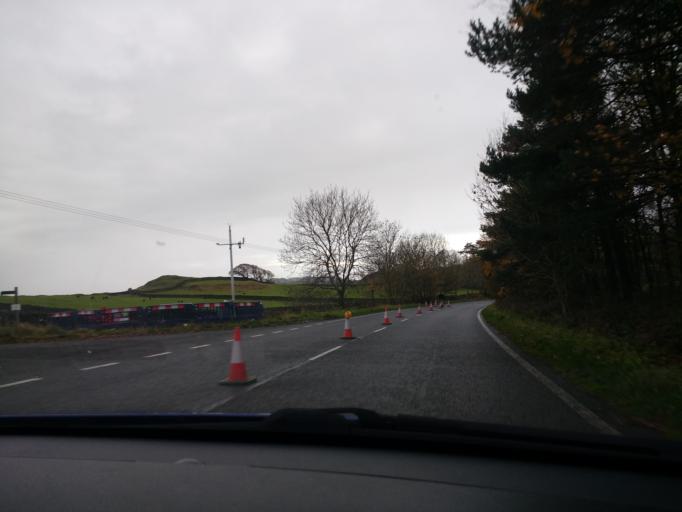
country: GB
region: England
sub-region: Cumbria
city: Millom
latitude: 54.2696
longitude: -3.2523
